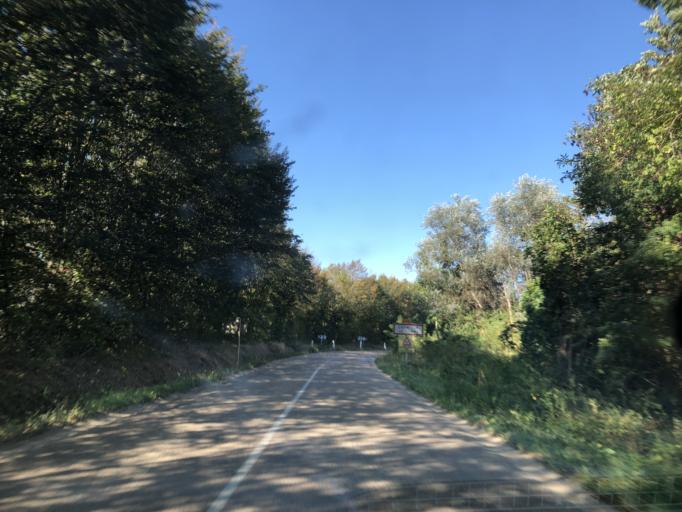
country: FR
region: Bourgogne
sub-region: Departement de l'Yonne
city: Gurgy
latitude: 47.8957
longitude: 3.5494
